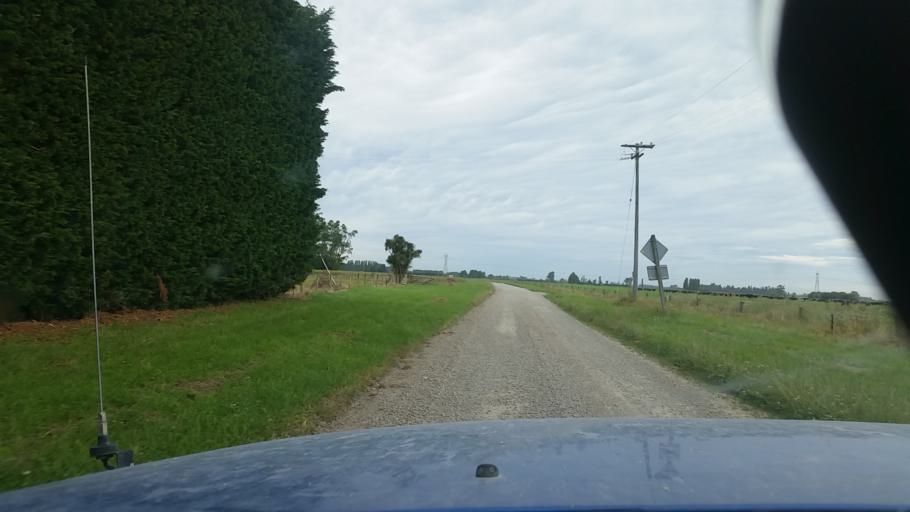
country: NZ
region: Canterbury
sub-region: Ashburton District
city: Ashburton
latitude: -43.8152
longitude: 171.6272
